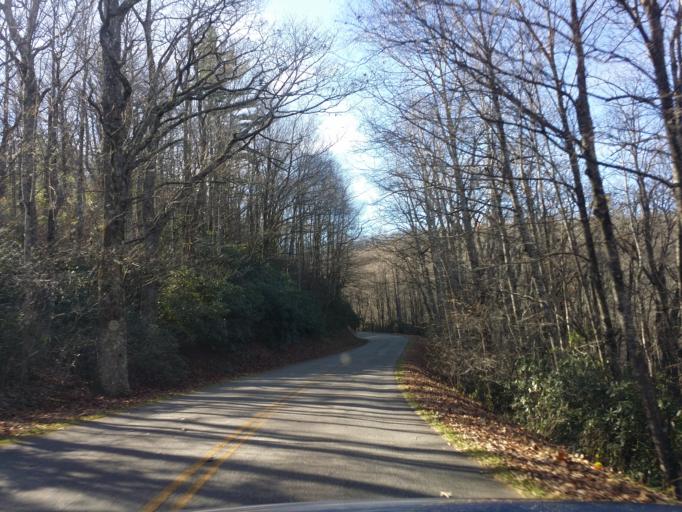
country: US
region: North Carolina
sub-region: McDowell County
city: West Marion
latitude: 35.7560
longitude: -82.1777
